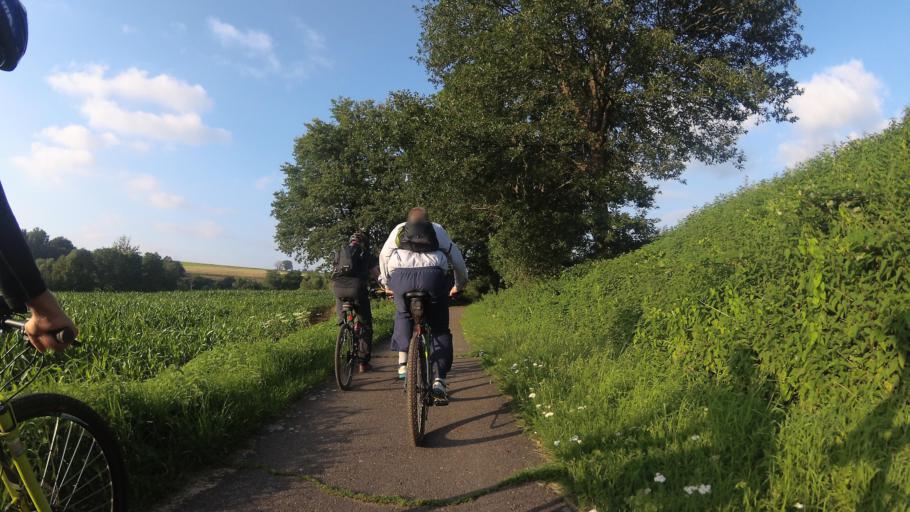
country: DE
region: Rheinland-Pfalz
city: Althornbach
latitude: 49.1948
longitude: 7.3578
